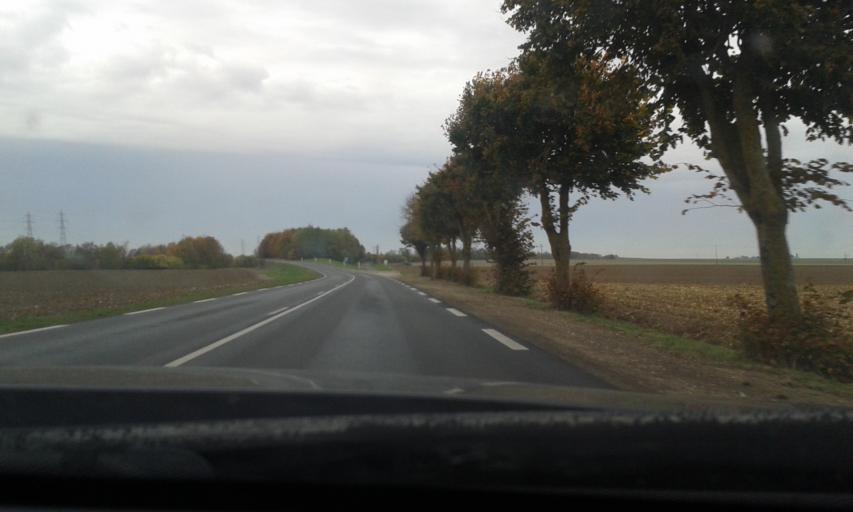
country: FR
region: Centre
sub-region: Departement d'Eure-et-Loir
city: Baigneaux
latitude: 48.1254
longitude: 1.8559
